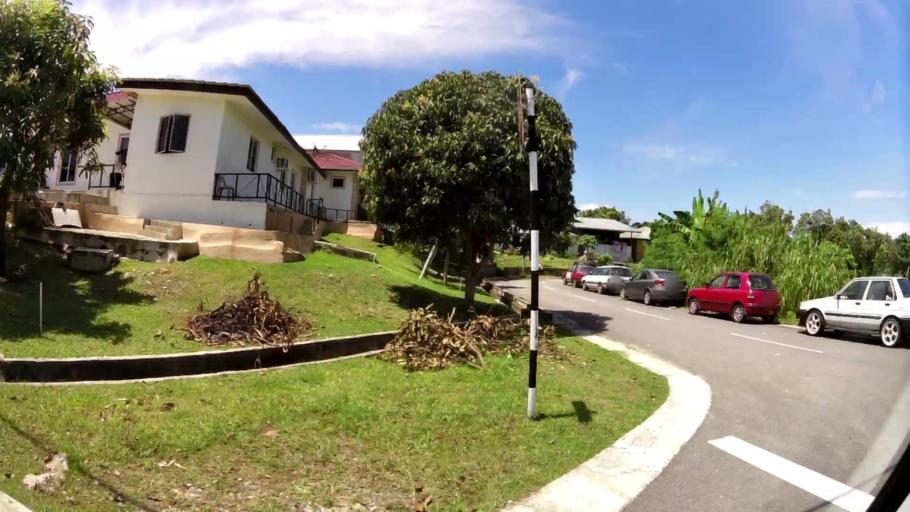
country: BN
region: Brunei and Muara
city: Bandar Seri Begawan
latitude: 4.9363
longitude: 114.9555
